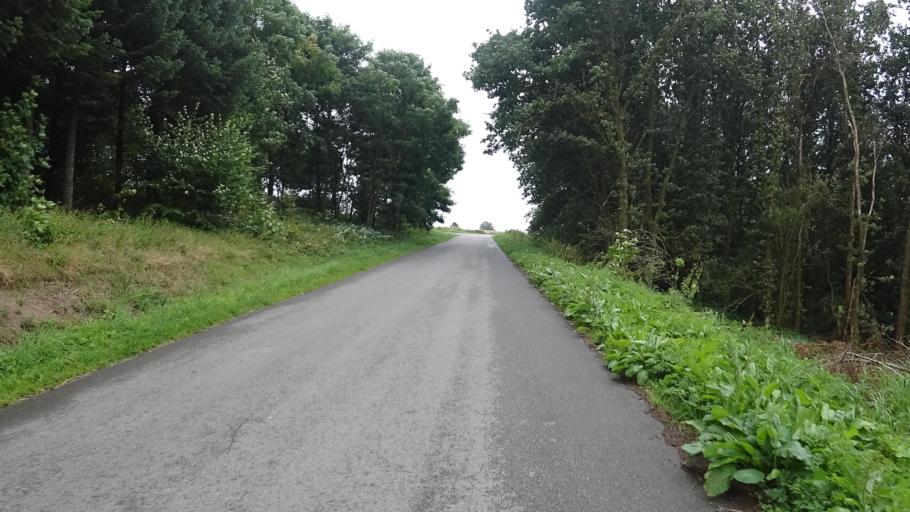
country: BE
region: Wallonia
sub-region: Province du Luxembourg
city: Chiny
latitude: 49.8008
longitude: 5.3739
